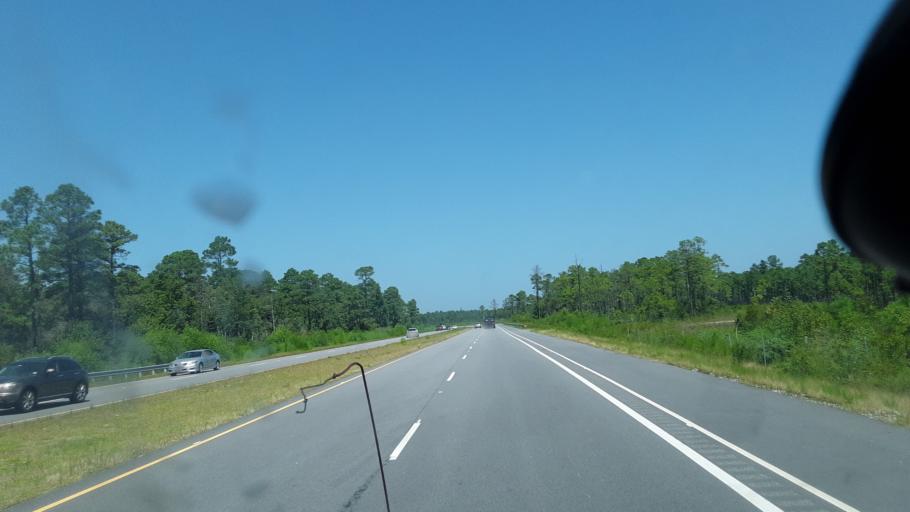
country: US
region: South Carolina
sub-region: Horry County
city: Forestbrook
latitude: 33.7943
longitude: -78.8825
